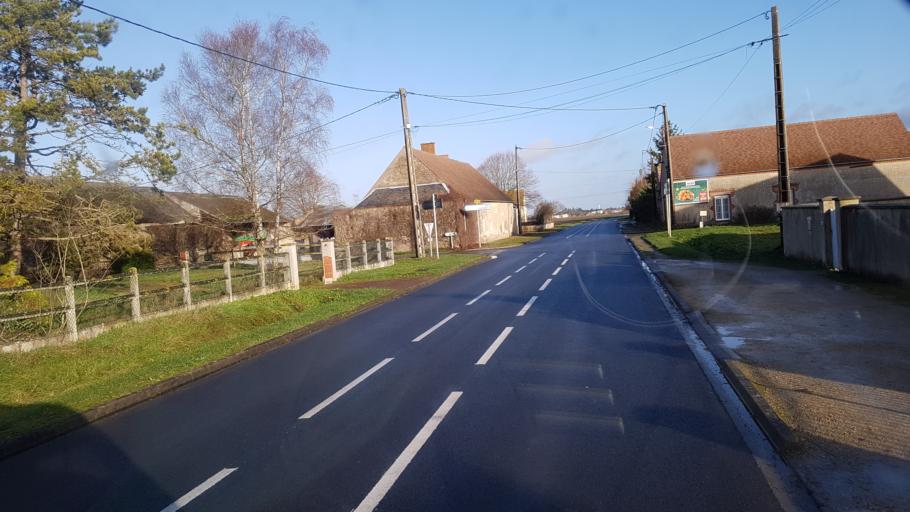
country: FR
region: Centre
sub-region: Departement du Loiret
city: Dadonville
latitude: 48.1055
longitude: 2.2455
